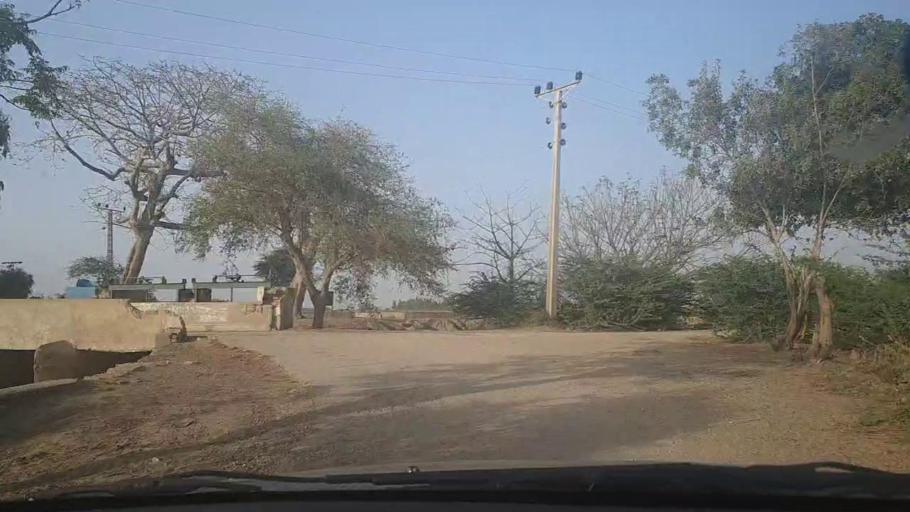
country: PK
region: Sindh
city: Keti Bandar
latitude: 24.2910
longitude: 67.6087
